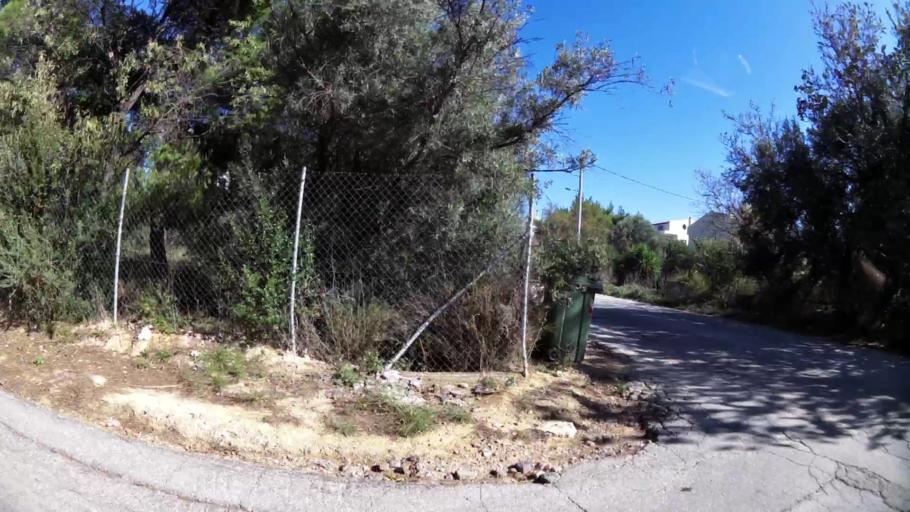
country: GR
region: Attica
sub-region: Nomarchia Athinas
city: Nea Erythraia
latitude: 38.0961
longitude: 23.7888
